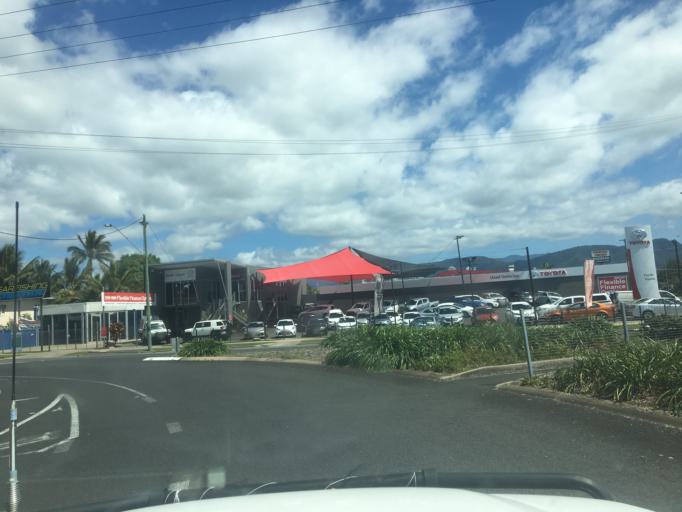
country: AU
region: Queensland
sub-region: Cairns
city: Cairns
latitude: -16.9238
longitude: 145.7665
